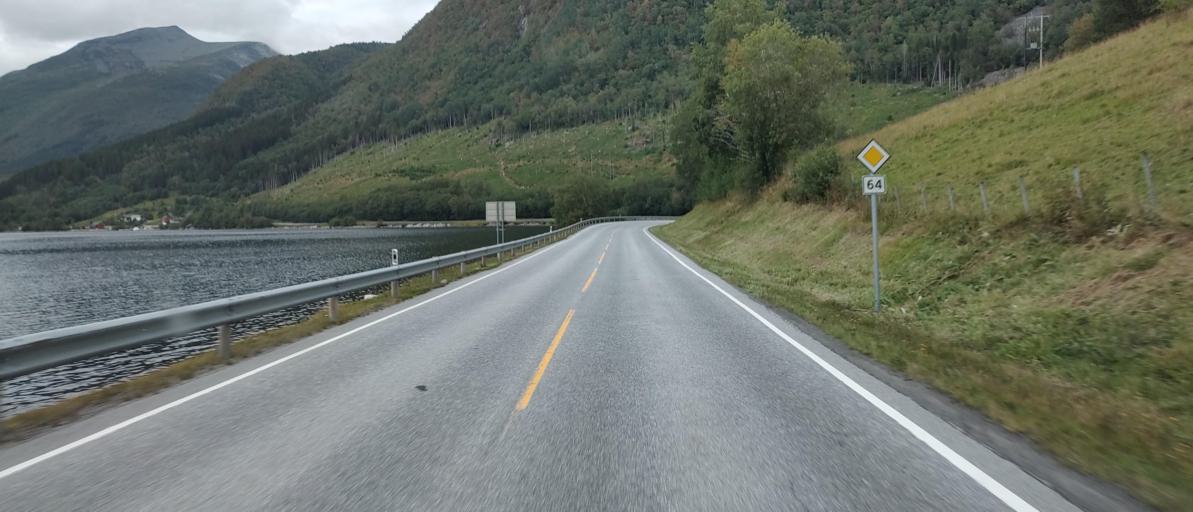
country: NO
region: More og Romsdal
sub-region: Rauma
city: Andalsnes
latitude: 62.5881
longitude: 7.5389
